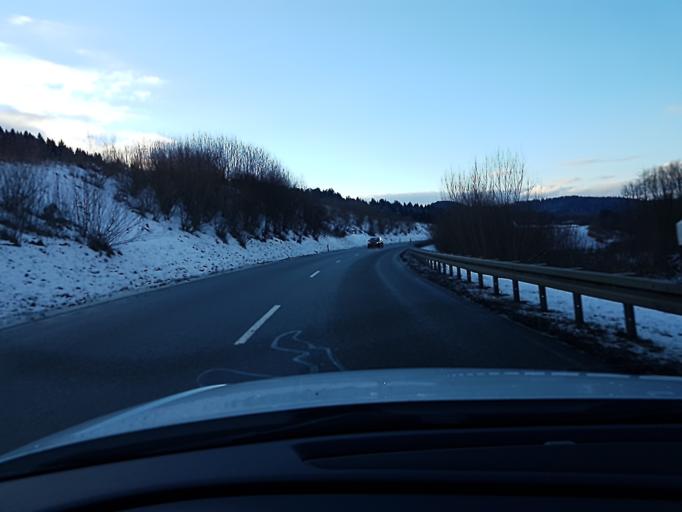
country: DE
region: Baden-Wuerttemberg
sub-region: Regierungsbezirk Stuttgart
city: Fichtenberg
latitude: 48.9841
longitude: 9.7047
